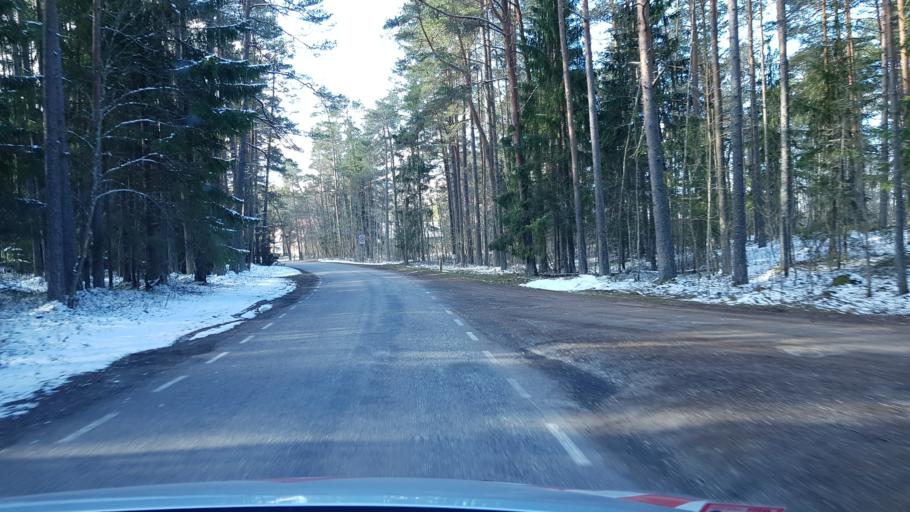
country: EE
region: Harju
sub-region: Loksa linn
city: Loksa
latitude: 59.5799
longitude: 25.9749
